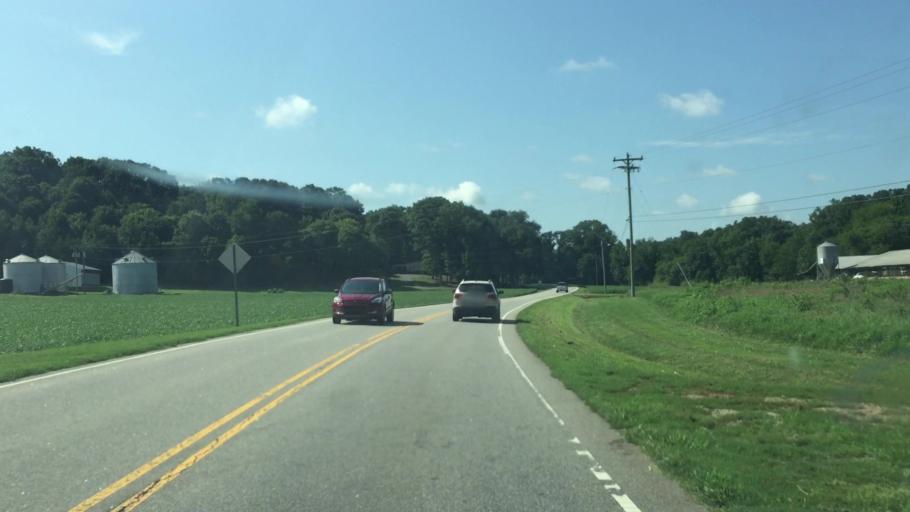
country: US
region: North Carolina
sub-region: Anson County
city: Burnsville
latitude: 35.1141
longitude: -80.3376
